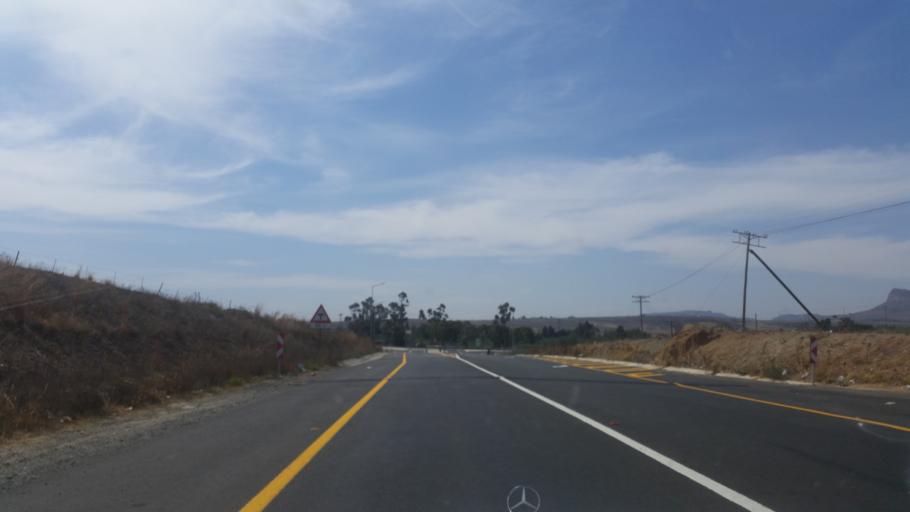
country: ZA
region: Orange Free State
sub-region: Thabo Mofutsanyana District Municipality
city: Harrismith
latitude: -28.2911
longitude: 29.0886
